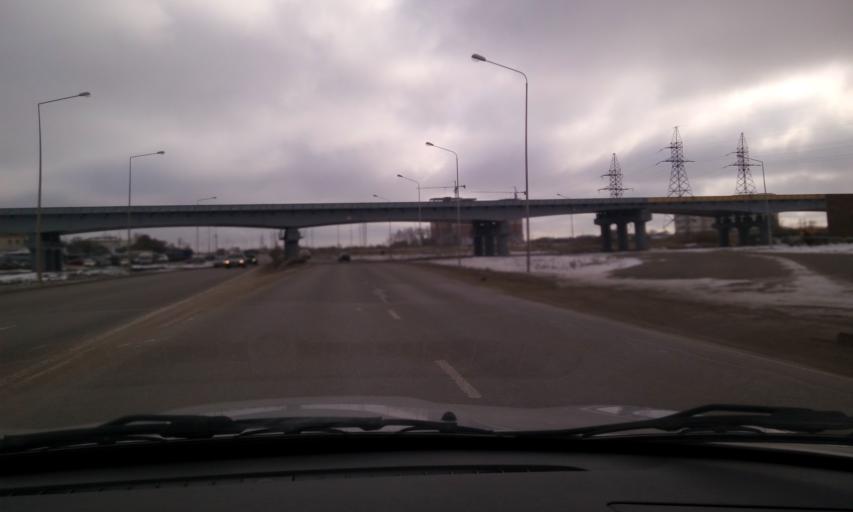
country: KZ
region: Astana Qalasy
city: Astana
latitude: 51.1372
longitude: 71.5318
